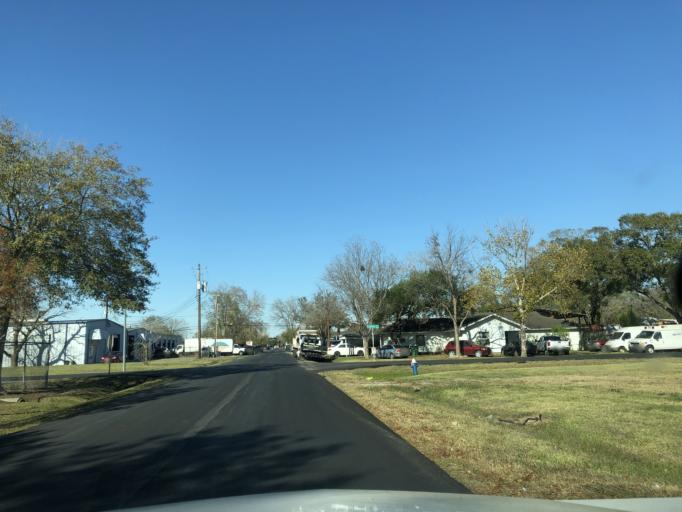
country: US
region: Texas
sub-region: Harris County
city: Bellaire
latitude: 29.6892
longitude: -95.4969
